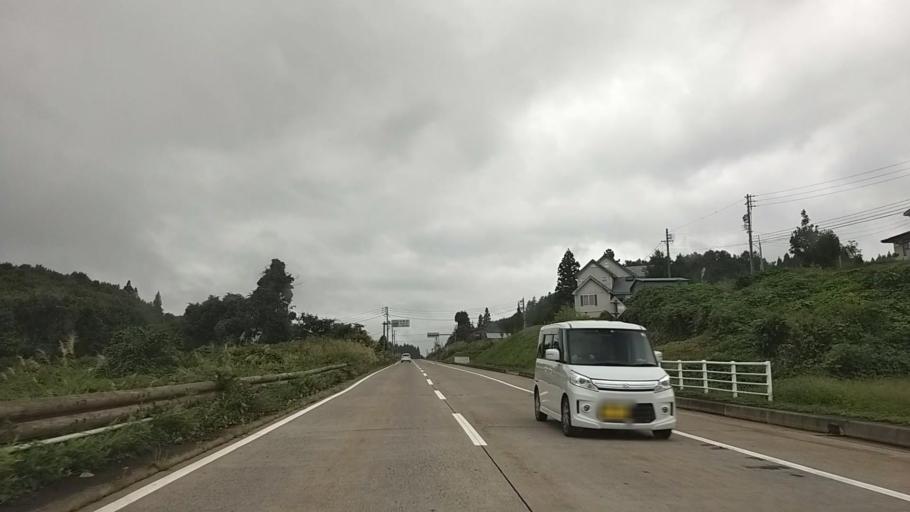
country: JP
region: Nagano
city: Iiyama
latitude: 36.8072
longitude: 138.3318
